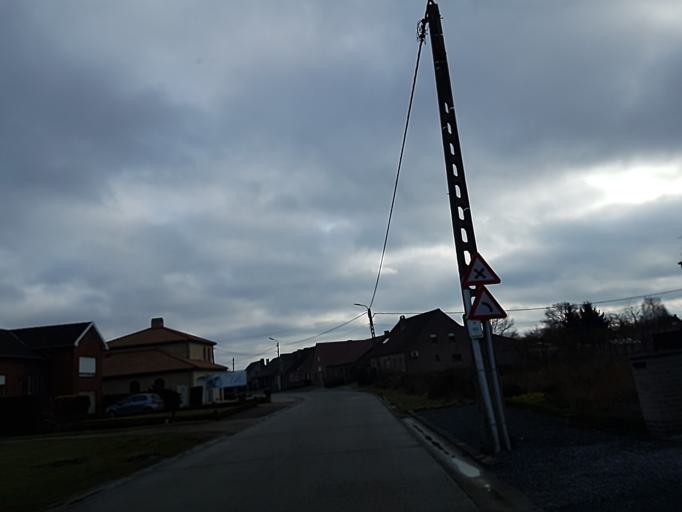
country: BE
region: Flanders
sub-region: Provincie Antwerpen
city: Hulshout
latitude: 51.0753
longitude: 4.8006
